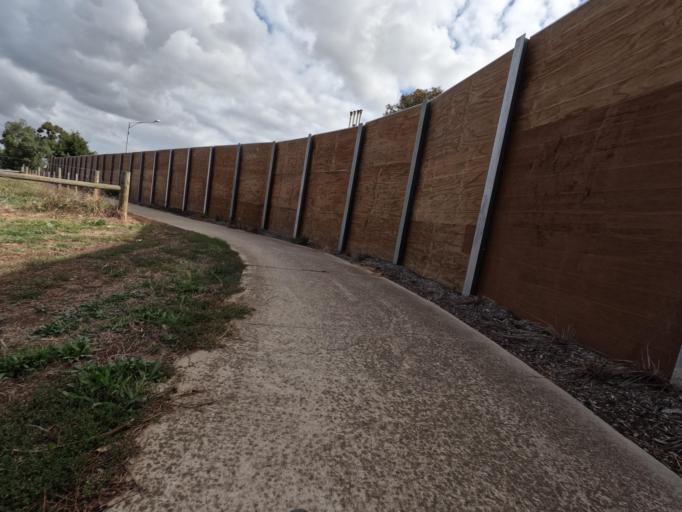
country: AU
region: Victoria
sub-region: Greater Geelong
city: Bell Post Hill
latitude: -38.0637
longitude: 144.3416
